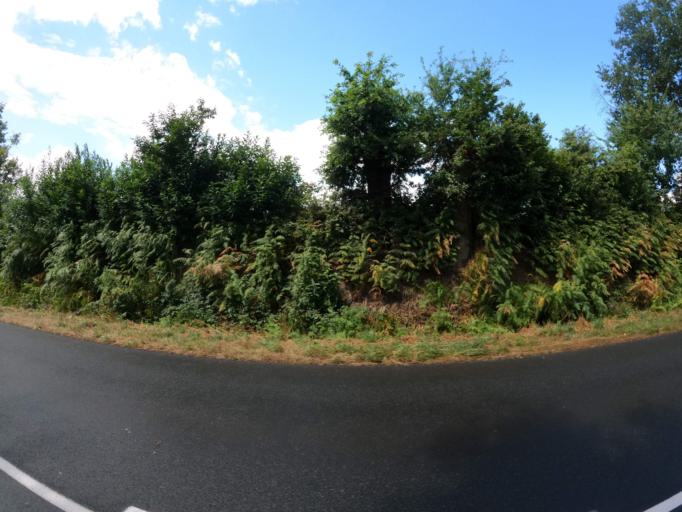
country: FR
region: Pays de la Loire
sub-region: Departement de Maine-et-Loire
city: Feneu
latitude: 47.6010
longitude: -0.5875
